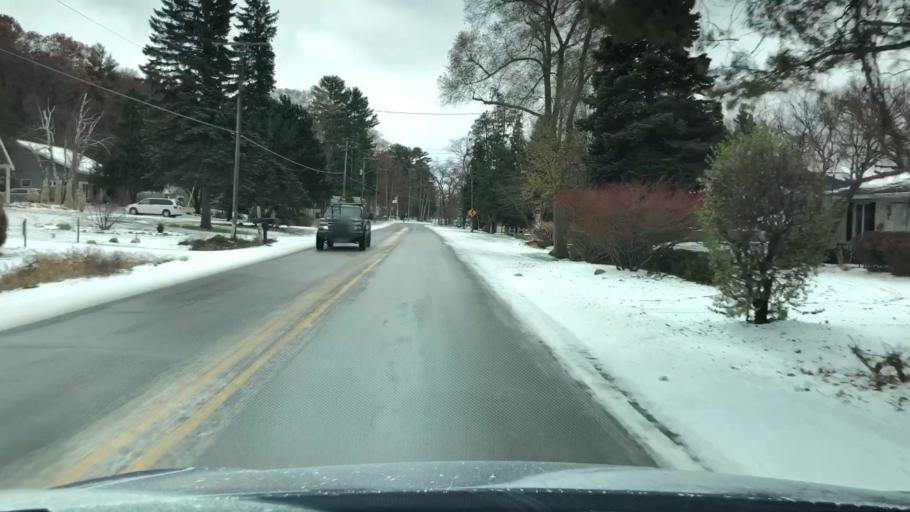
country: US
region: Michigan
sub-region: Grand Traverse County
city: Traverse City
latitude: 44.7948
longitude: -85.5857
